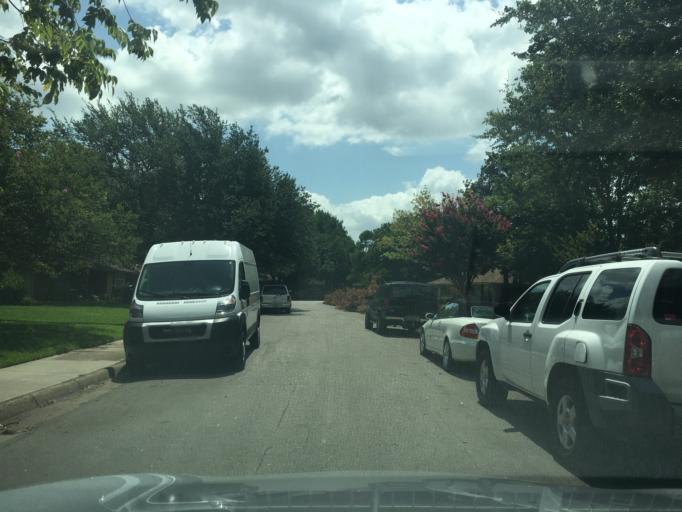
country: US
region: Texas
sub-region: Dallas County
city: Addison
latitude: 32.9222
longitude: -96.8219
